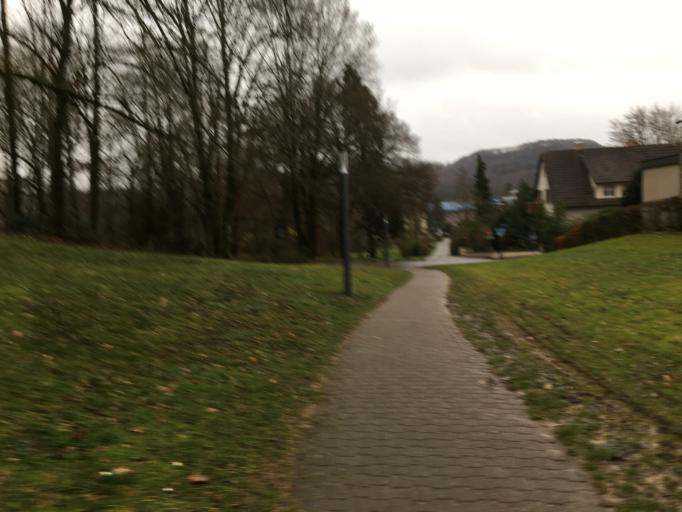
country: DE
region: Baden-Wuerttemberg
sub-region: Freiburg Region
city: Bad Sackingen
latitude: 47.5590
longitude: 7.9398
